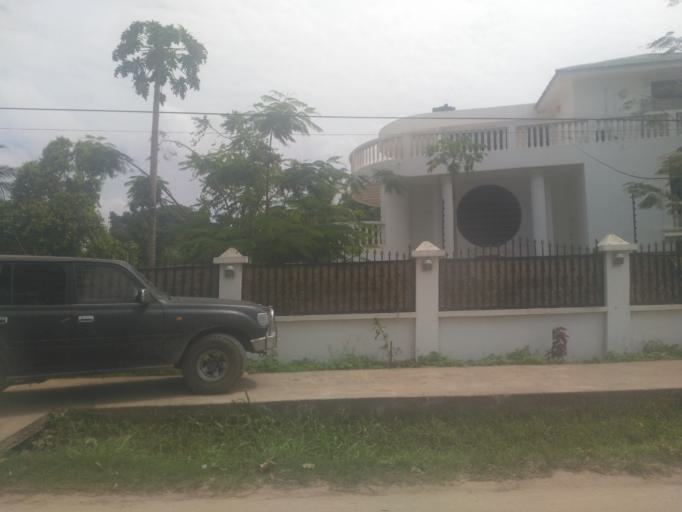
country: TZ
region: Zanzibar Urban/West
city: Zanzibar
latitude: -6.2087
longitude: 39.2162
